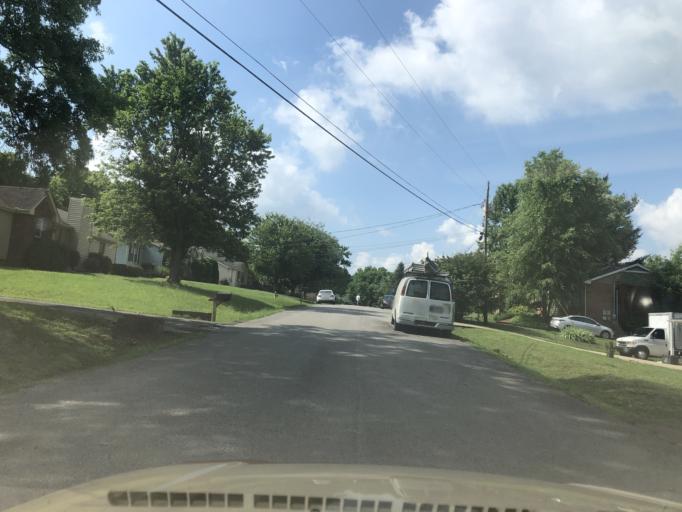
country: US
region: Tennessee
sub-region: Wilson County
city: Green Hill
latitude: 36.2410
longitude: -86.5880
